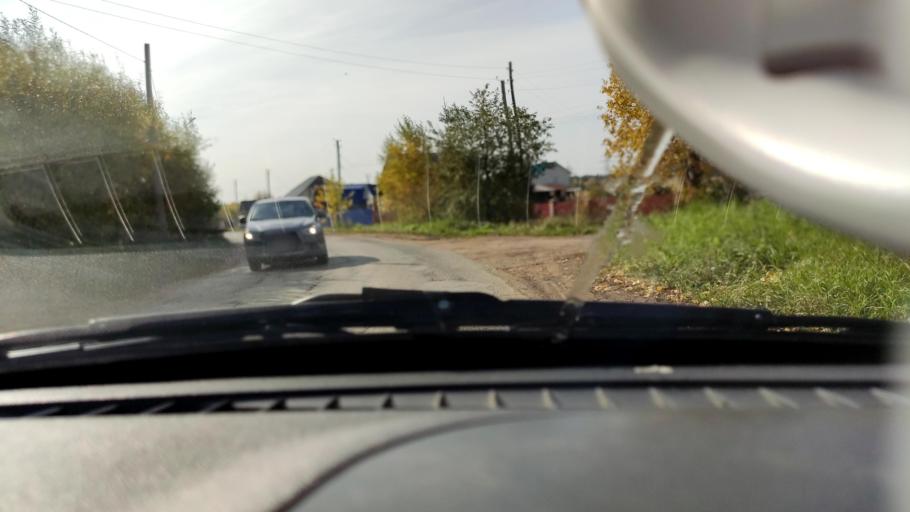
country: RU
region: Perm
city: Overyata
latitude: 58.0766
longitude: 55.8876
